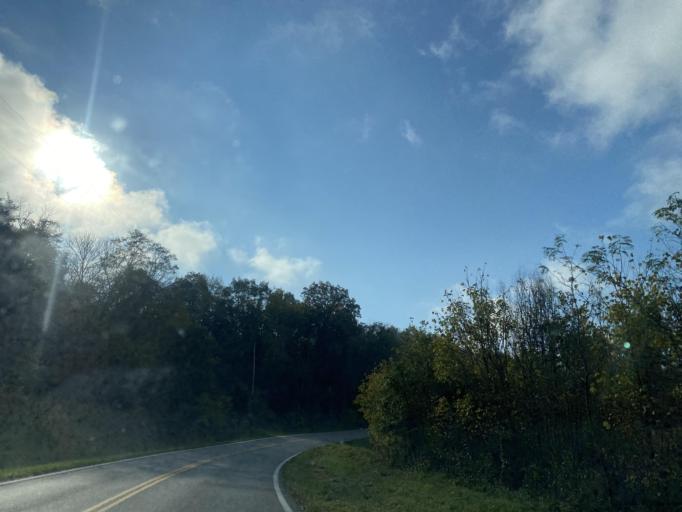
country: US
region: Kentucky
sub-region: Pendleton County
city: Falmouth
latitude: 38.7102
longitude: -84.3023
